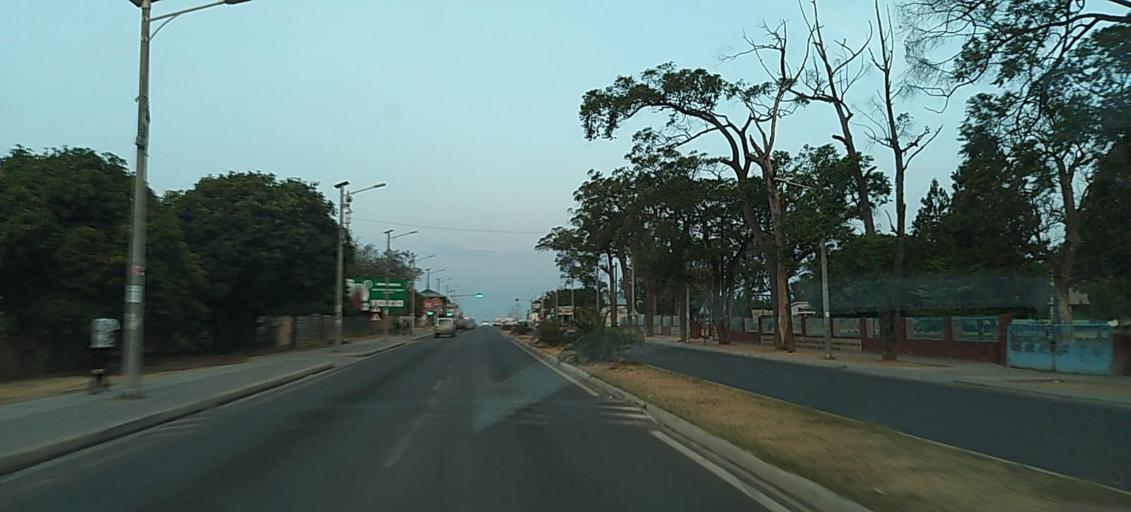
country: ZM
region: Copperbelt
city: Chingola
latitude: -12.5466
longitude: 27.8617
